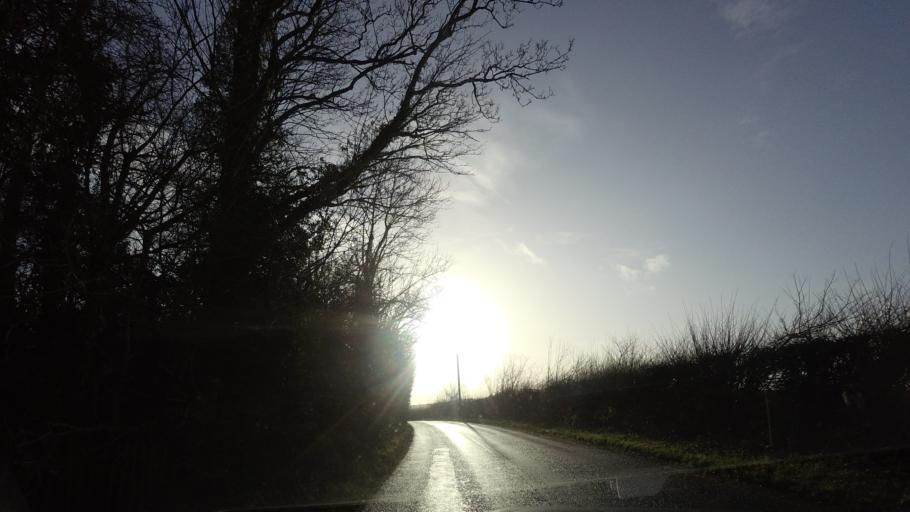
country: GB
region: England
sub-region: Kent
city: Borough Green
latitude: 51.2956
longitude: 0.2846
